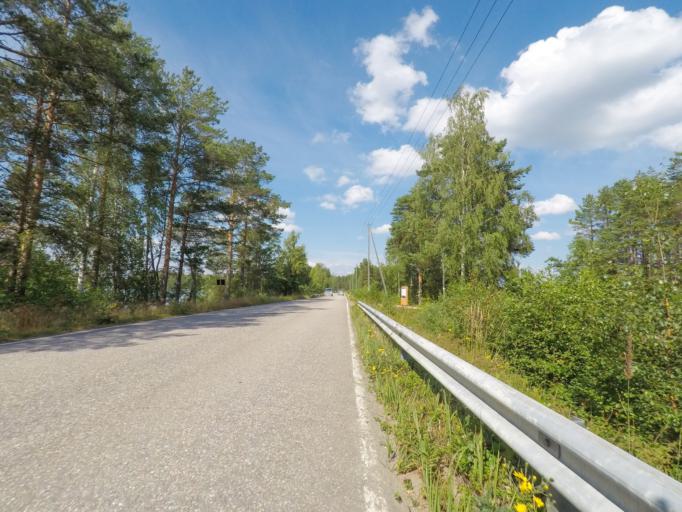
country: FI
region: Southern Savonia
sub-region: Mikkeli
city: Puumala
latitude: 61.4900
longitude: 28.1667
